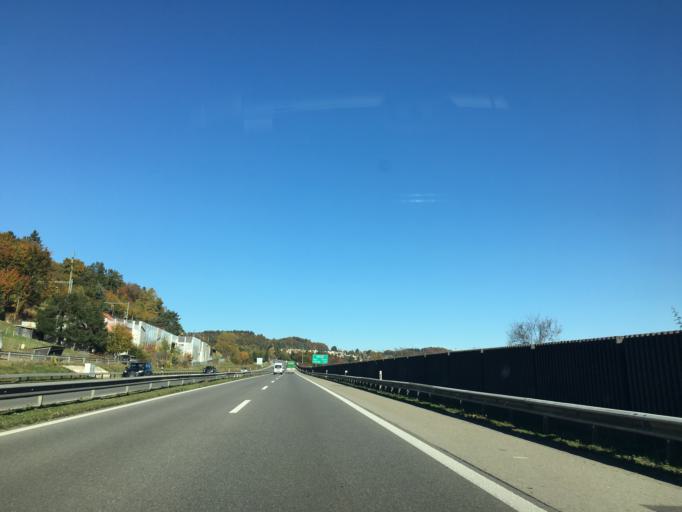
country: CH
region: Fribourg
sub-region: Sarine District
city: Matran
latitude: 46.7874
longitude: 7.0950
